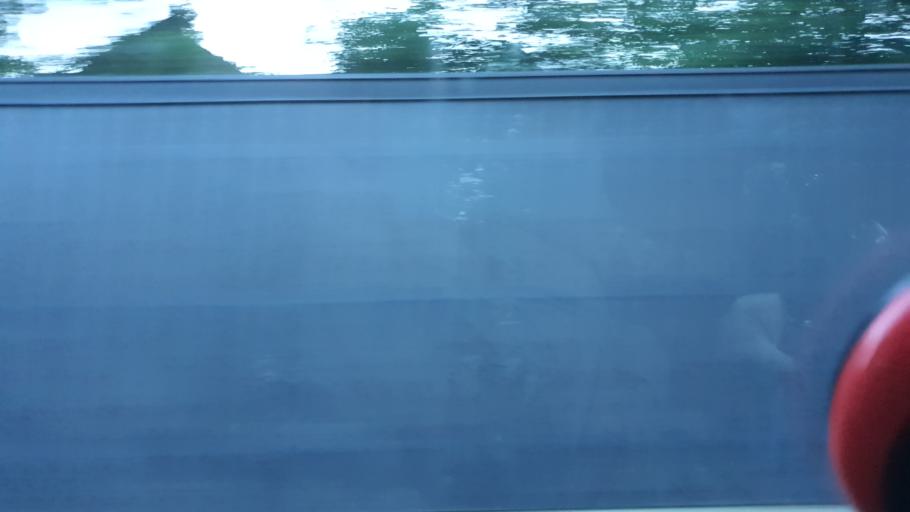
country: GB
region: Northern Ireland
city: Rostrevor
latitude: 54.0784
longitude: -6.1831
